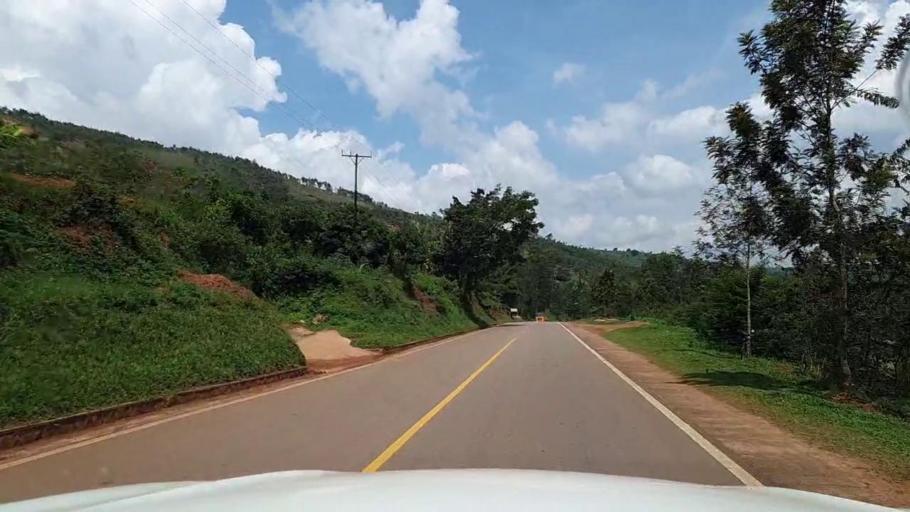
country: RW
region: Kigali
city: Kigali
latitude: -1.8354
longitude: 30.0800
